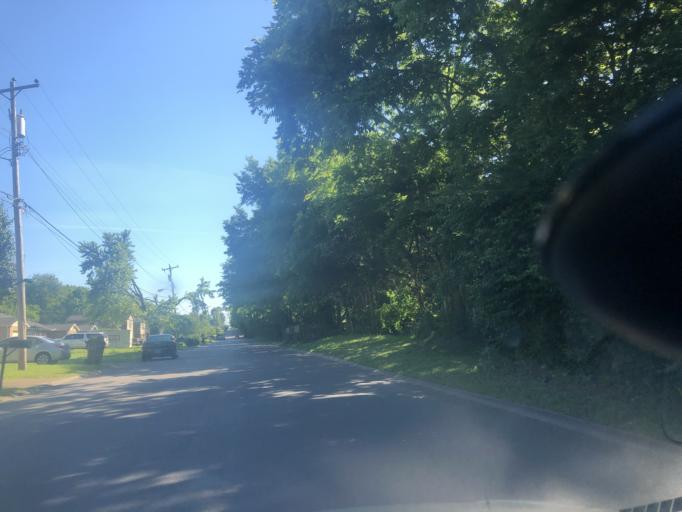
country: US
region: Tennessee
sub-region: Davidson County
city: Lakewood
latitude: 36.2412
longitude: -86.6711
